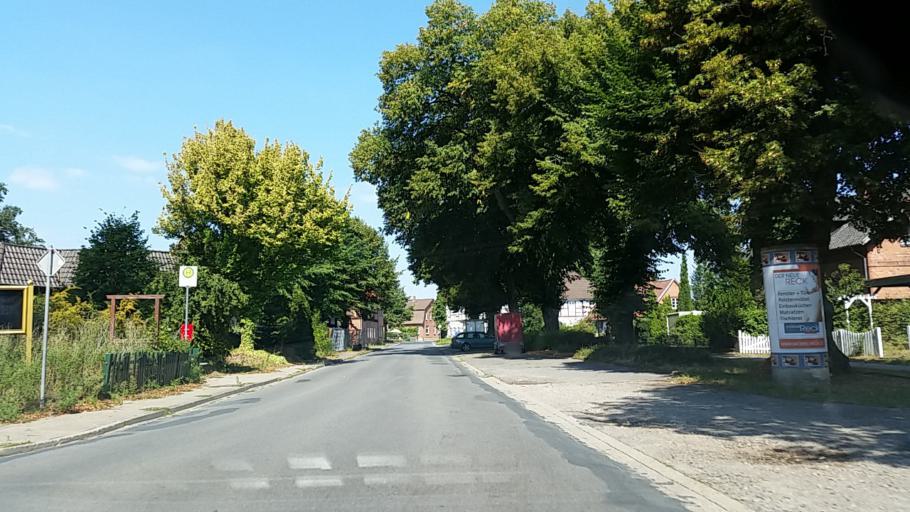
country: DE
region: Lower Saxony
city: Bad Bevensen
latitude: 53.0877
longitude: 10.5630
